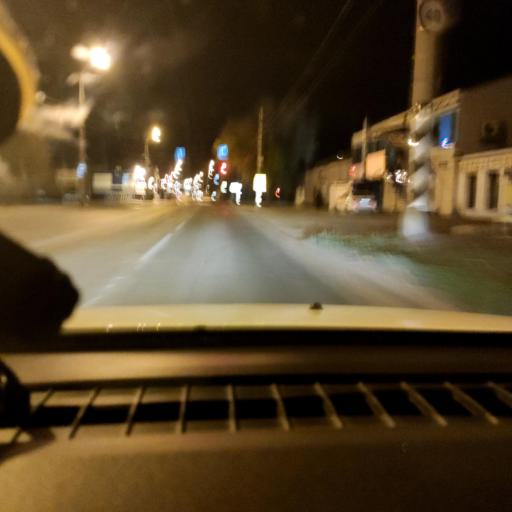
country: RU
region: Samara
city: Rozhdestveno
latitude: 53.1654
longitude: 50.0745
